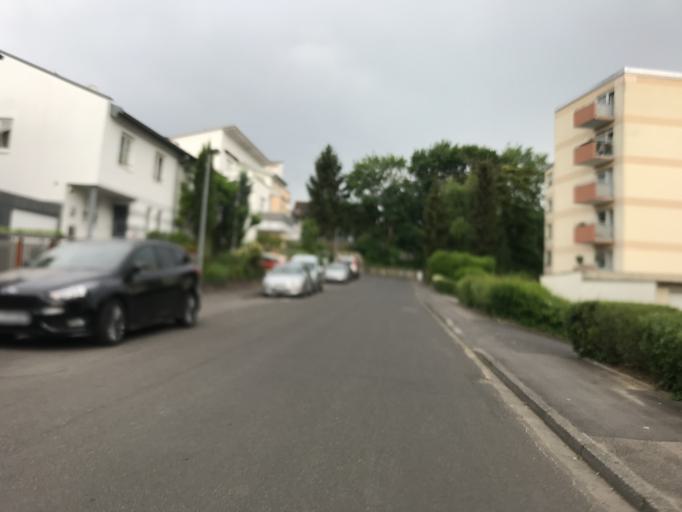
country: DE
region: Rheinland-Pfalz
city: Budenheim
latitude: 50.0184
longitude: 8.1670
